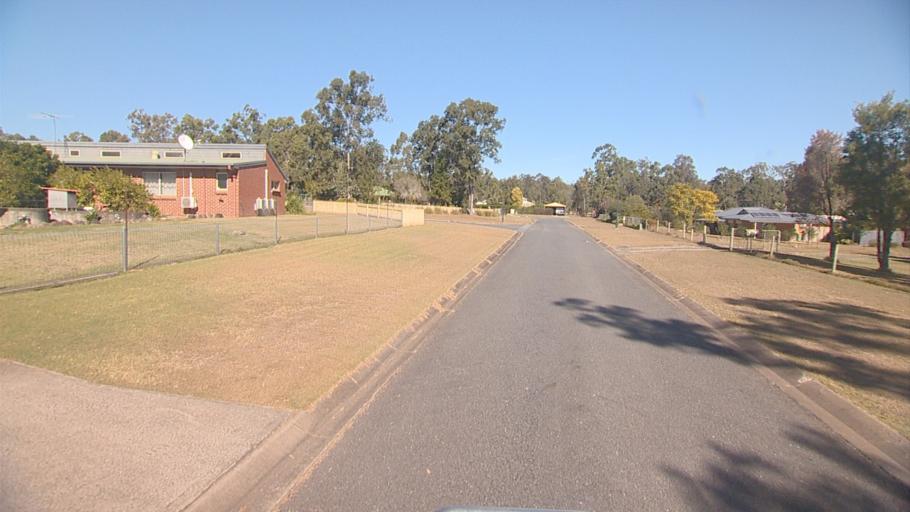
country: AU
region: Queensland
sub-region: Logan
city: North Maclean
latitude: -27.8204
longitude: 152.9502
